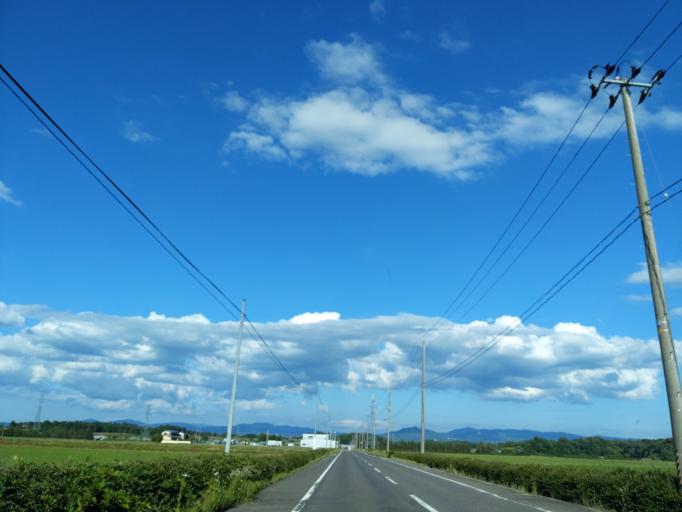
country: JP
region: Fukushima
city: Sukagawa
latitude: 37.3277
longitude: 140.3310
